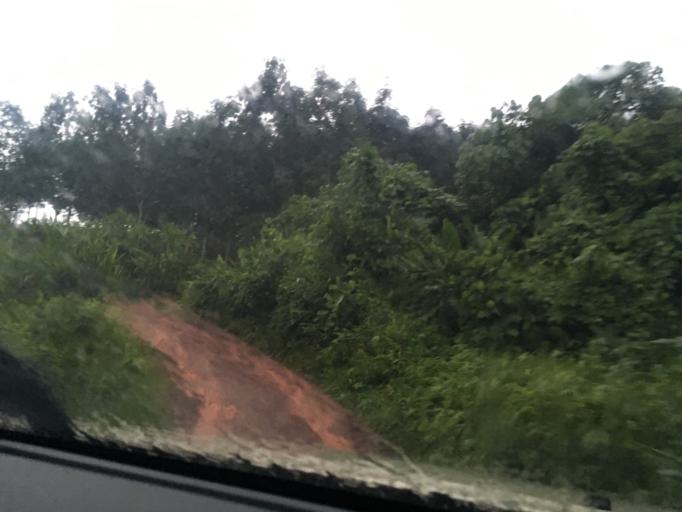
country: LA
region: Oudomxai
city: Muang La
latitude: 21.2423
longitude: 101.9438
